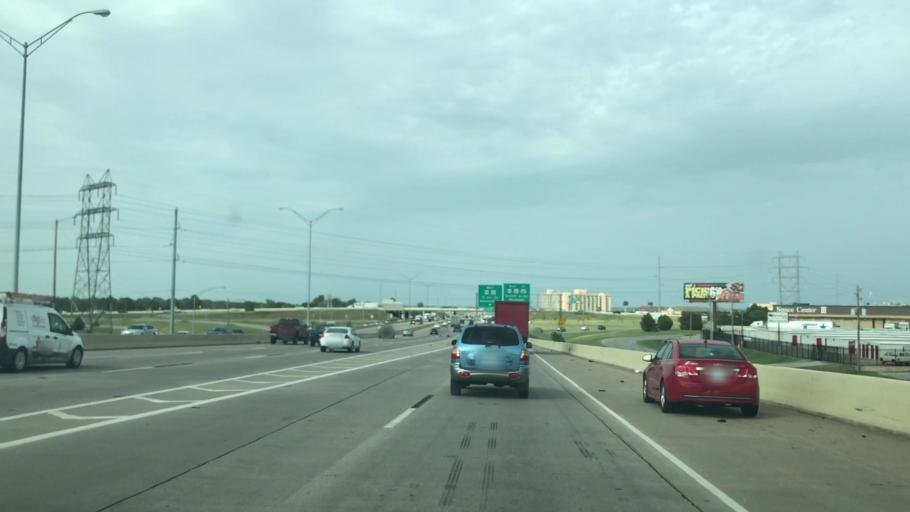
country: US
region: Oklahoma
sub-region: Tulsa County
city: Tulsa
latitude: 36.1104
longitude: -95.9008
